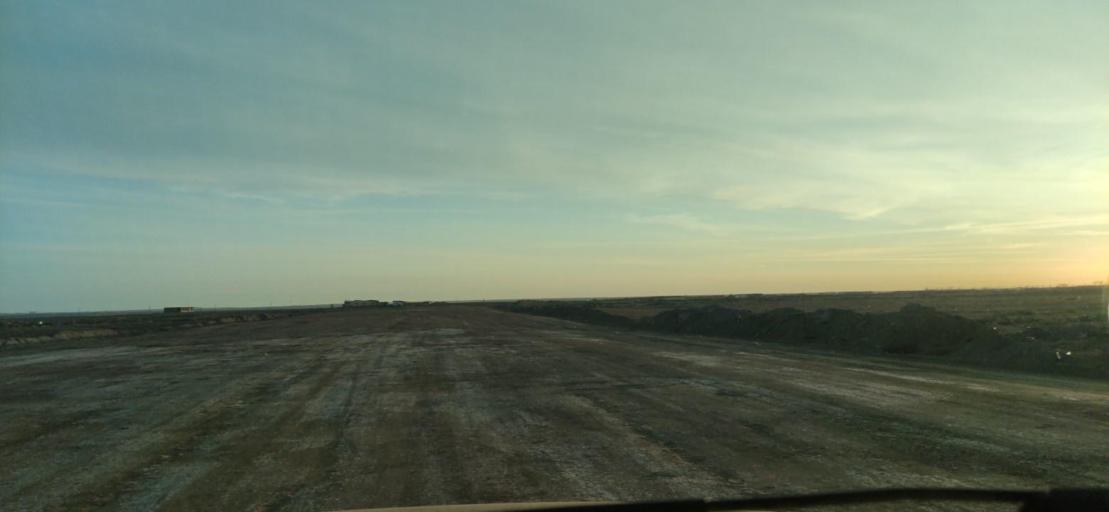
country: KZ
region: Qaraghandy
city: Saryshaghan
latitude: 46.0177
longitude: 73.5894
